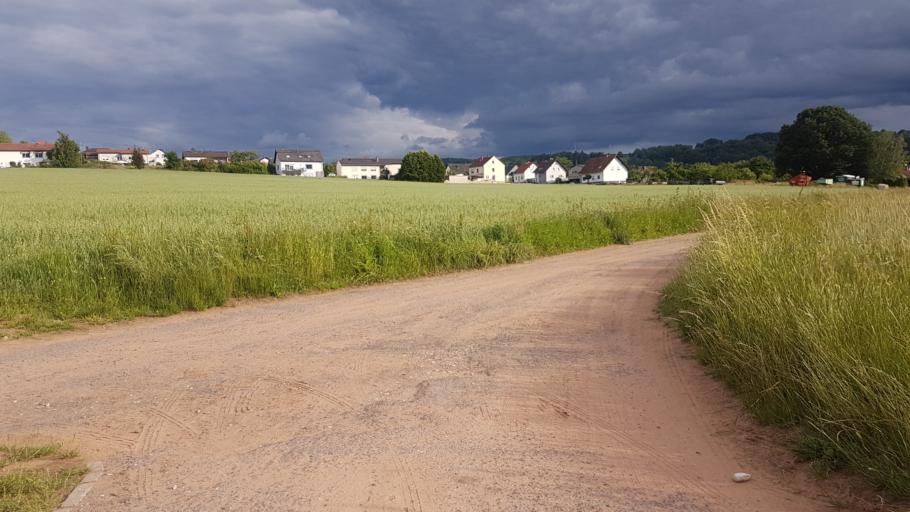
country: DE
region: Saarland
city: Britten
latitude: 49.4854
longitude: 6.7025
